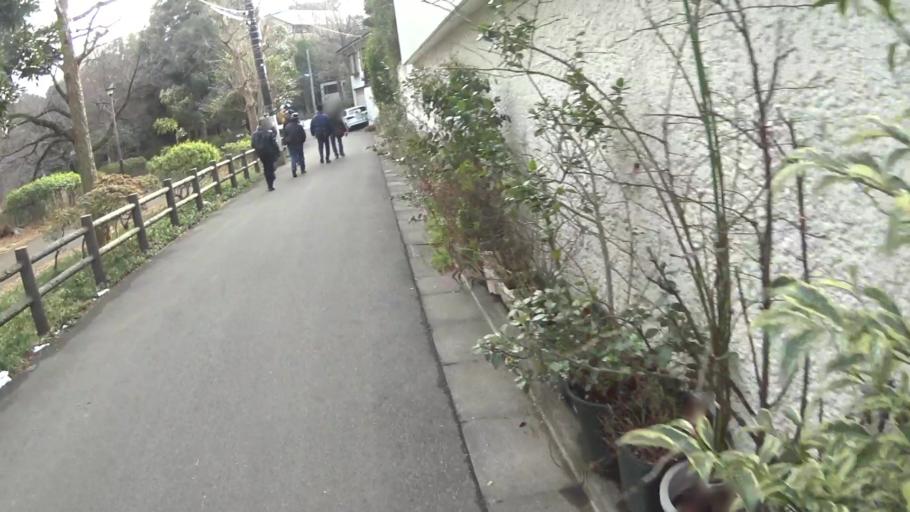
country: JP
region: Tokyo
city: Musashino
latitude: 35.7132
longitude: 139.5911
